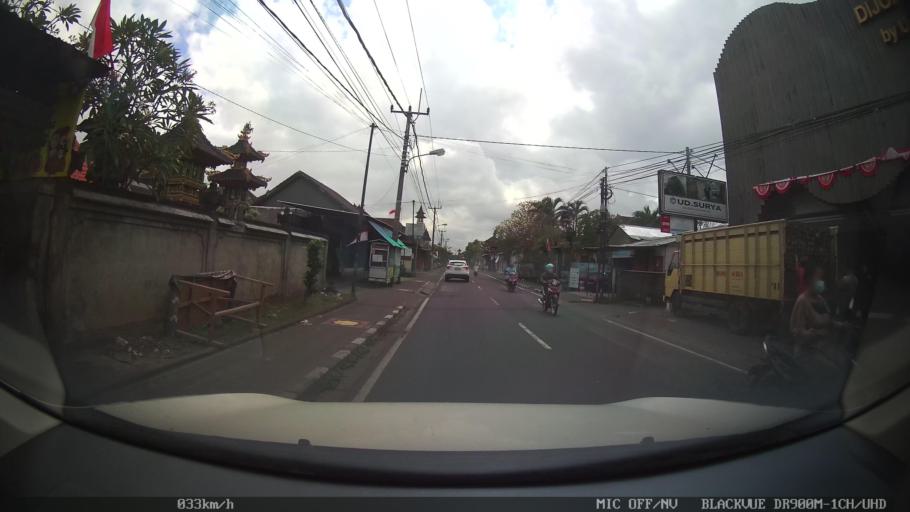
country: ID
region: Bali
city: Banjar Pekenjelodan
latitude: -8.5954
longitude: 115.1740
